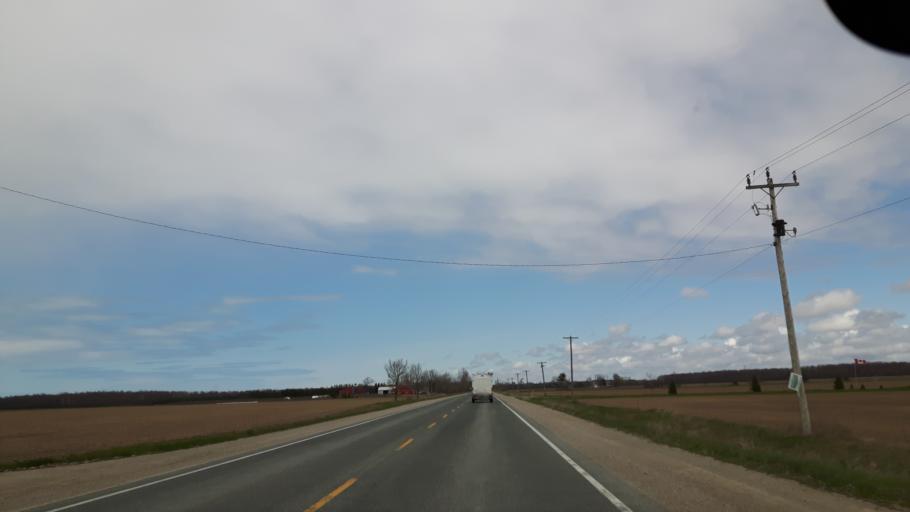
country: CA
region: Ontario
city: Bluewater
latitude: 43.5175
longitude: -81.6934
